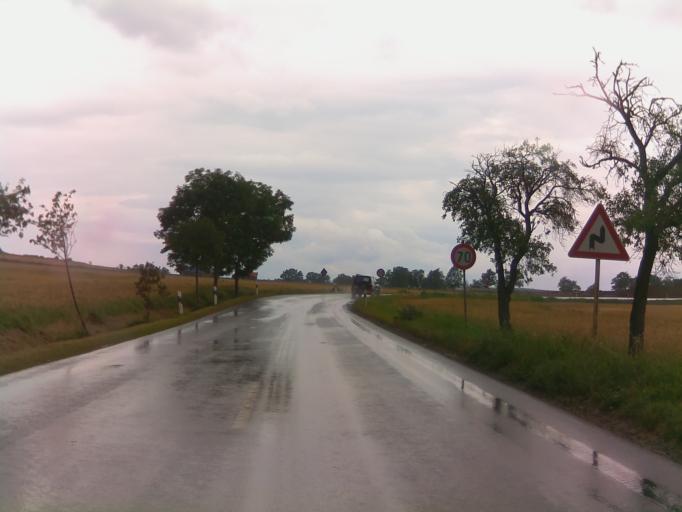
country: DE
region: Thuringia
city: Stadtilm
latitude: 50.7449
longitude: 11.0769
